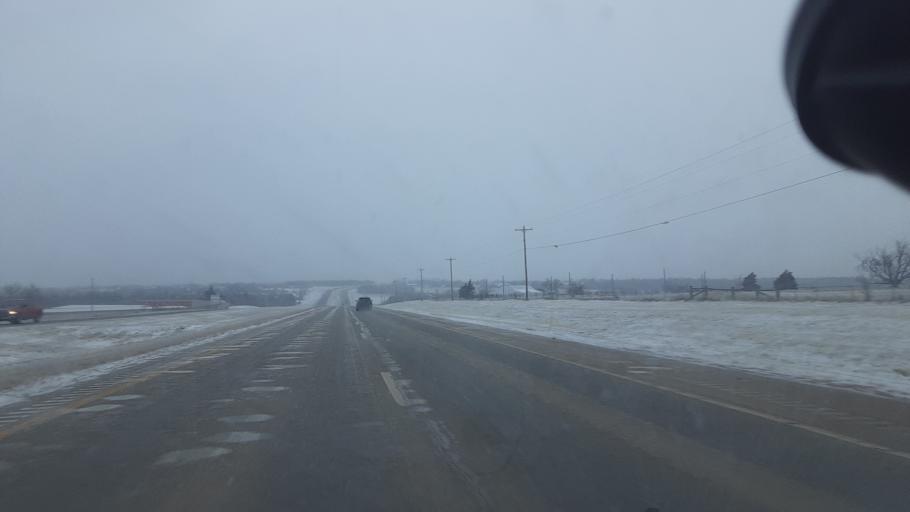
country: US
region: Oklahoma
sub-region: Logan County
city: Guthrie
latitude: 35.8943
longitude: -97.3607
